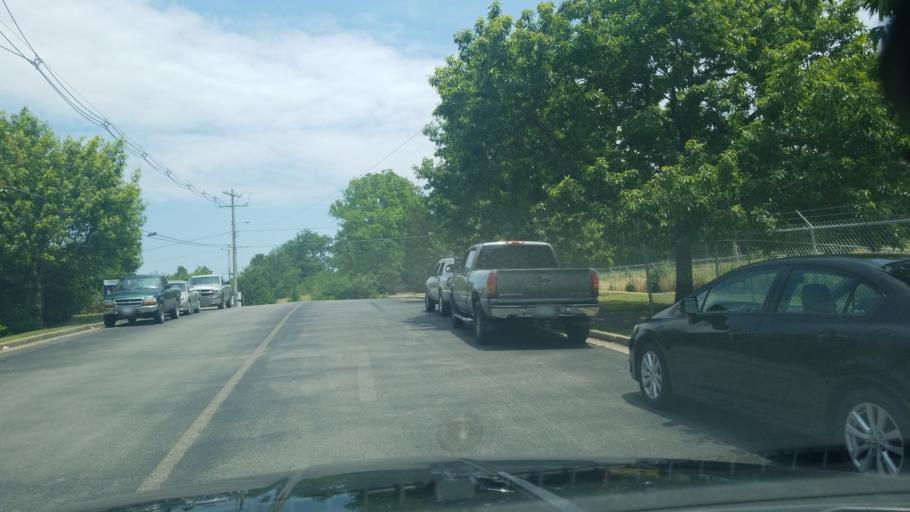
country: US
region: Tennessee
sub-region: Davidson County
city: Goodlettsville
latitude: 36.2478
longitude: -86.7488
